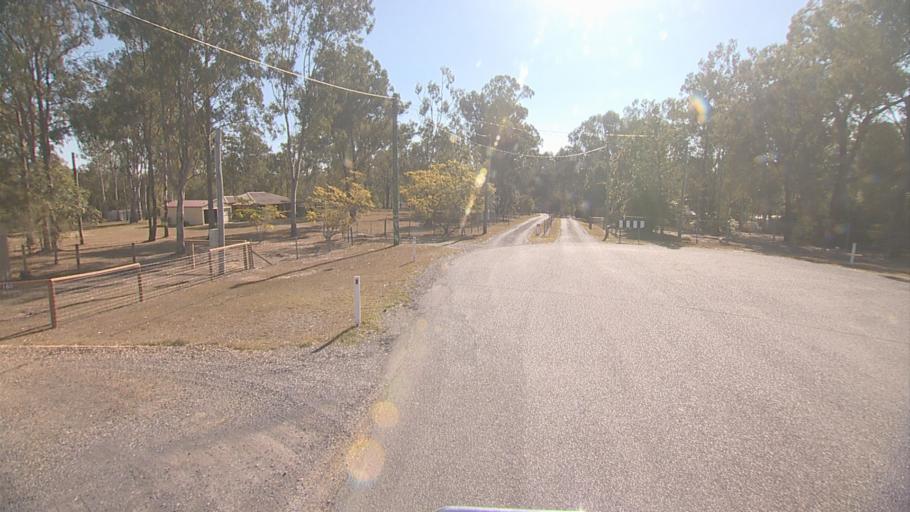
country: AU
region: Queensland
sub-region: Logan
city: North Maclean
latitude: -27.8208
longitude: 153.0422
